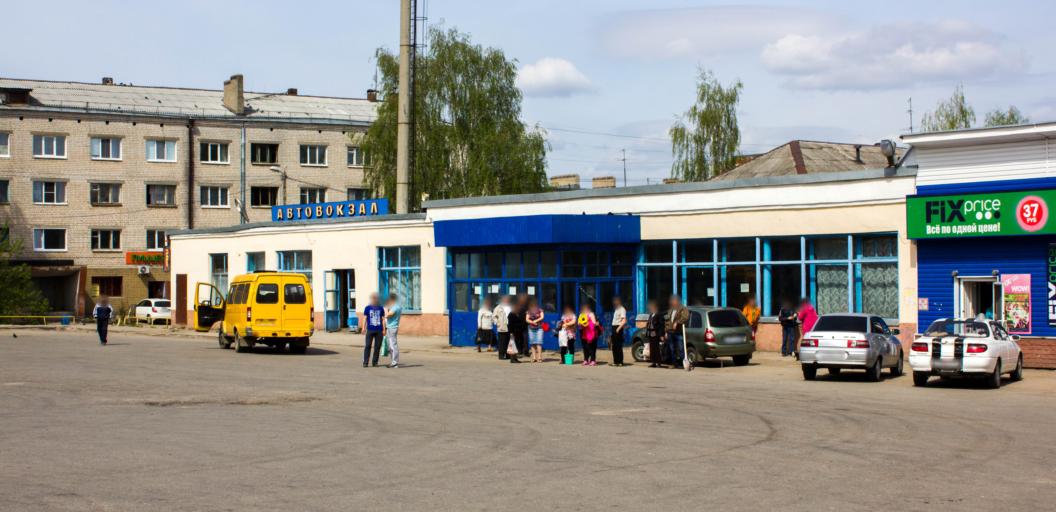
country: RU
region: Nizjnij Novgorod
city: Lyskovo
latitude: 56.0136
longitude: 45.0326
